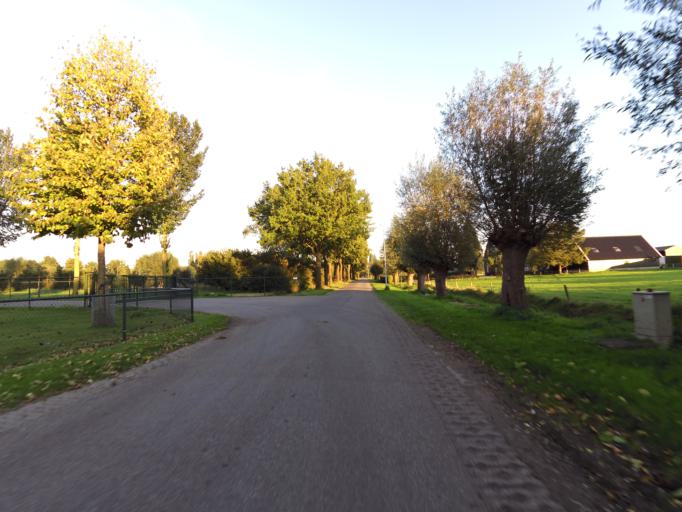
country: NL
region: Gelderland
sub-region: Gemeente Doesburg
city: Doesburg
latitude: 51.9211
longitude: 6.1657
